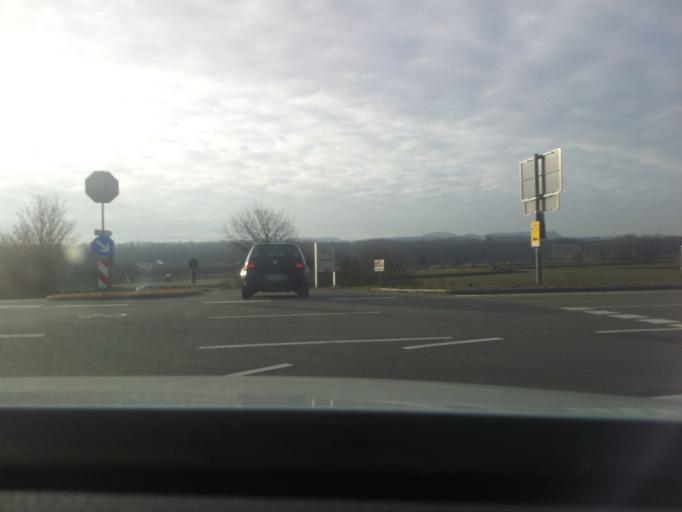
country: DE
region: Baden-Wuerttemberg
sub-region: Tuebingen Region
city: Kusterdingen
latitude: 48.4963
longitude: 9.1278
